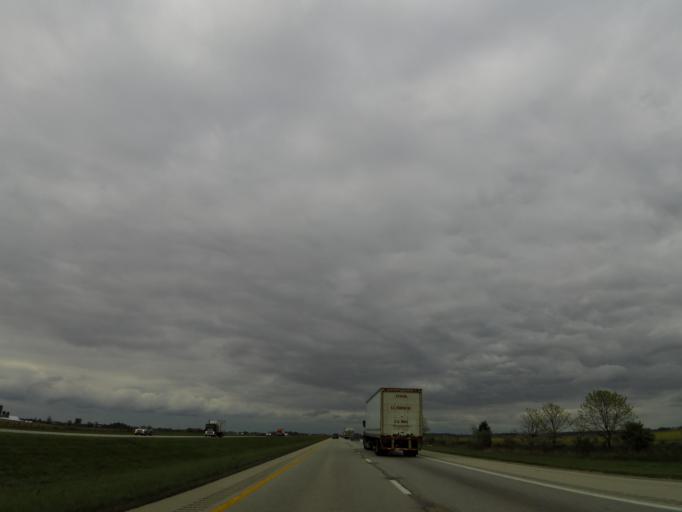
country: US
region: Ohio
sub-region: Clinton County
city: Wilmington
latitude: 39.5379
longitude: -83.7780
